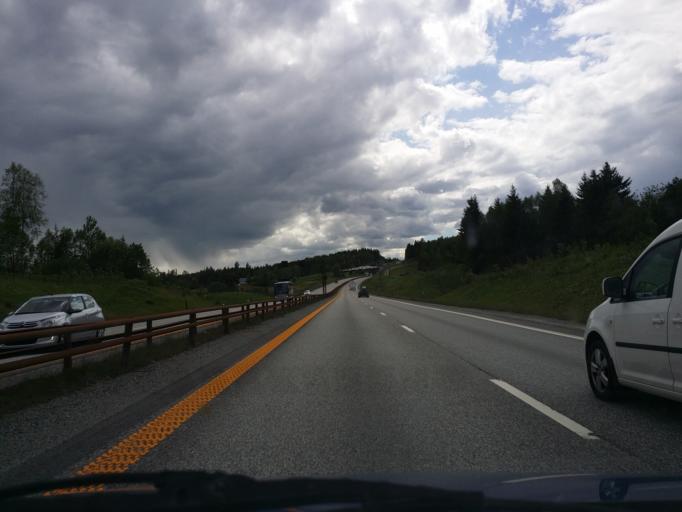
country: NO
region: Akershus
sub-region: Eidsvoll
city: Raholt
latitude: 60.3258
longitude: 11.1812
